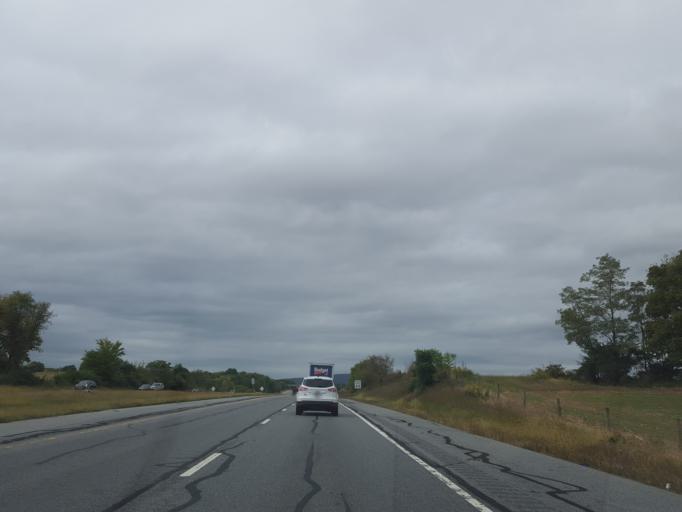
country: US
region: Maryland
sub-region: Frederick County
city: Brunswick
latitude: 39.3565
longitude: -77.5895
